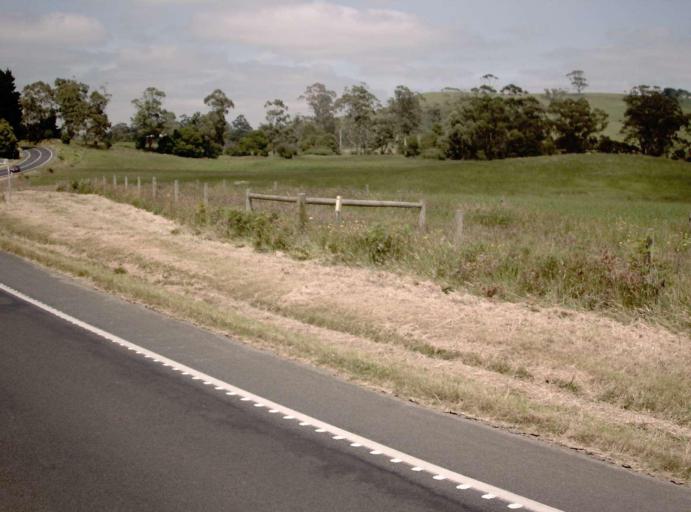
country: AU
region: Victoria
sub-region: Baw Baw
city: Warragul
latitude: -38.4306
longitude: 146.0367
